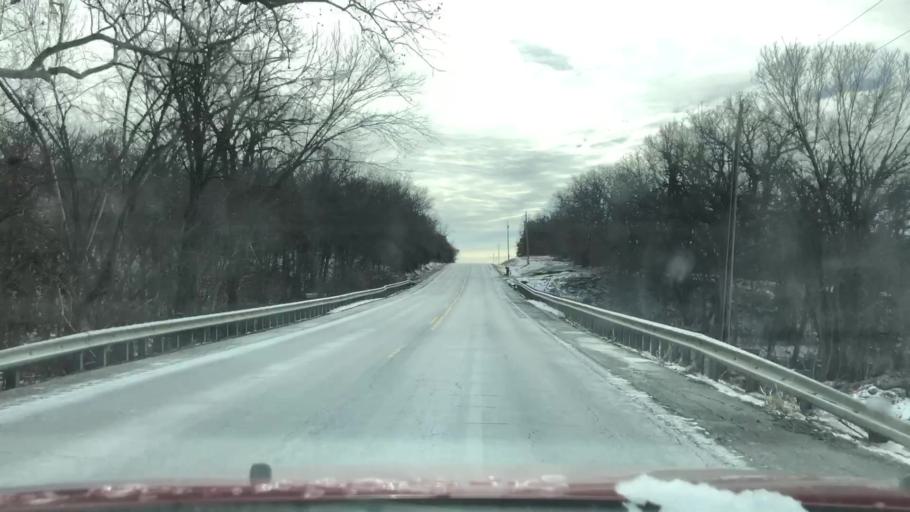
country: US
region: Missouri
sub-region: Jackson County
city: Lone Jack
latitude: 38.9116
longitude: -94.1333
